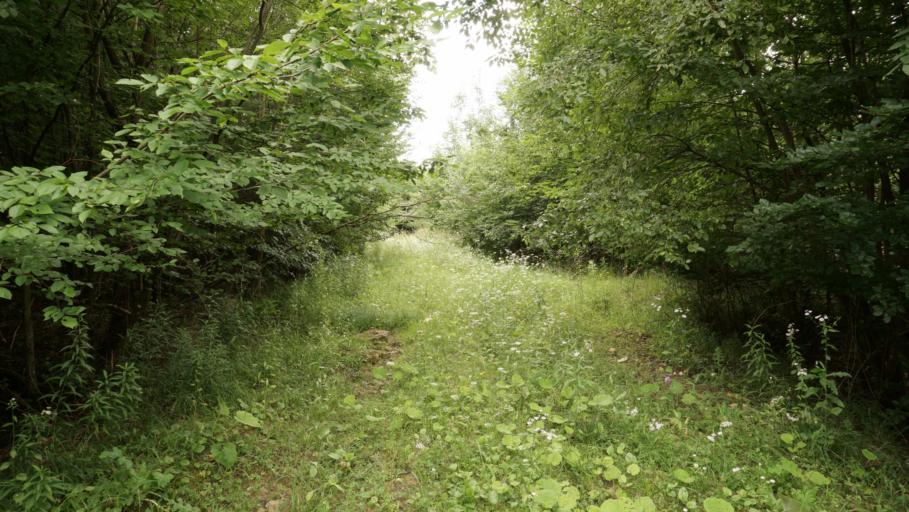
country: DE
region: Baden-Wuerttemberg
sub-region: Karlsruhe Region
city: Hassmersheim
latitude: 49.3188
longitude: 9.1555
